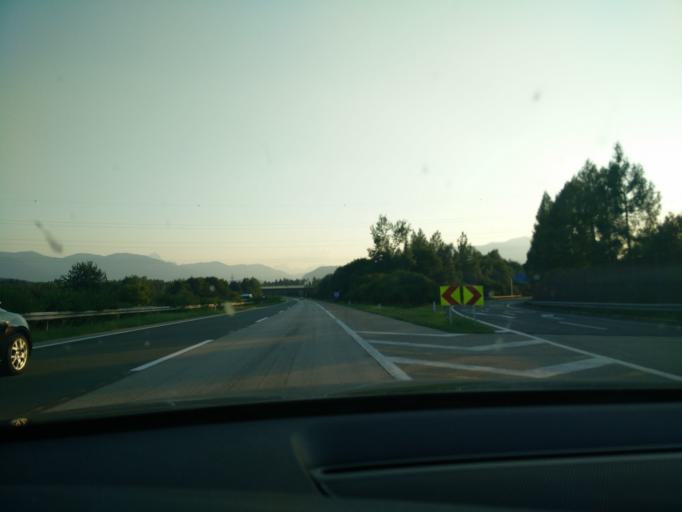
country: AT
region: Carinthia
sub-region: Politischer Bezirk Villach Land
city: Wernberg
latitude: 46.6208
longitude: 13.9096
